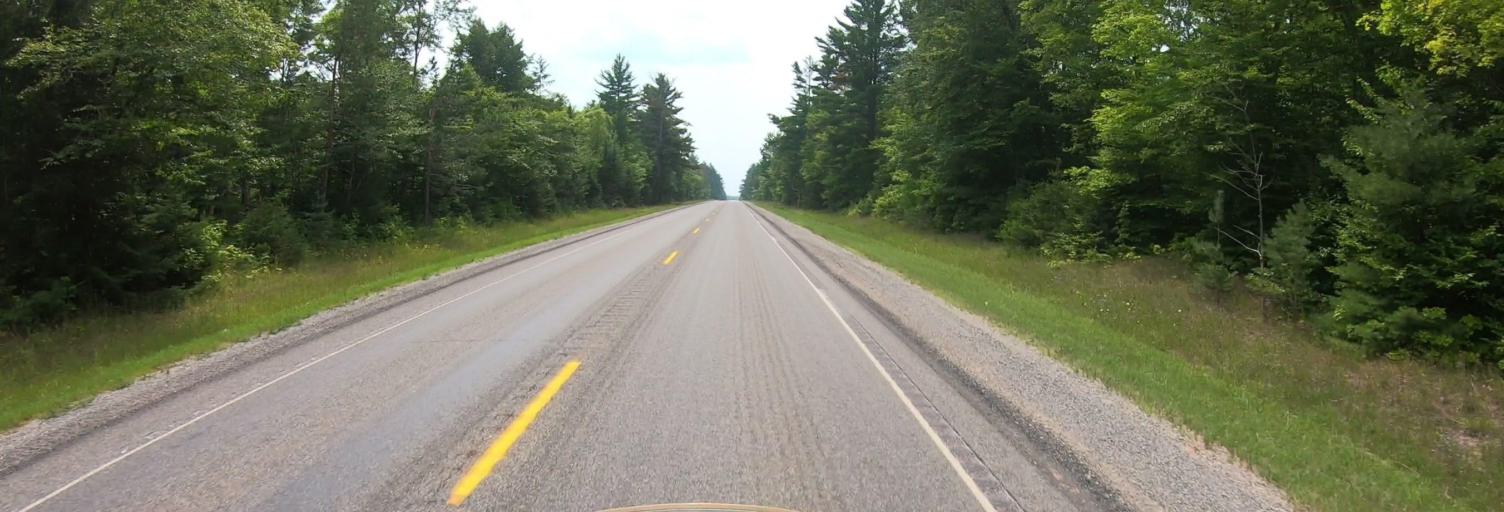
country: US
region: Michigan
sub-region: Alger County
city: Munising
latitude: 46.3519
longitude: -86.7240
